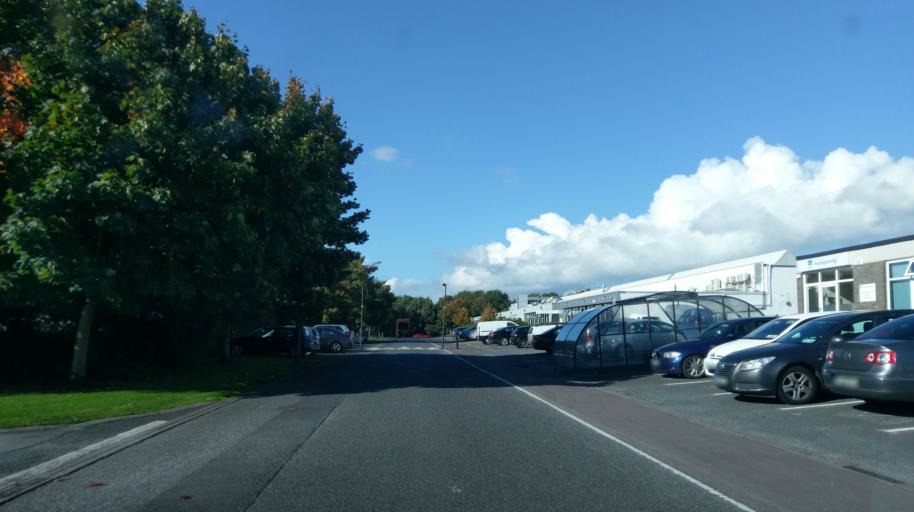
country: IE
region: Connaught
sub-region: County Galway
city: Gaillimh
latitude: 53.2854
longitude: -9.0278
